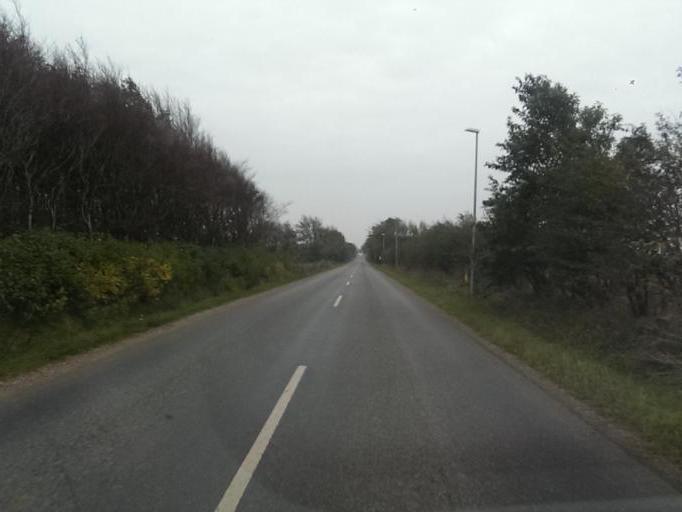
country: DK
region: South Denmark
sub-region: Esbjerg Kommune
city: Tjaereborg
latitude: 55.4828
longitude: 8.5553
